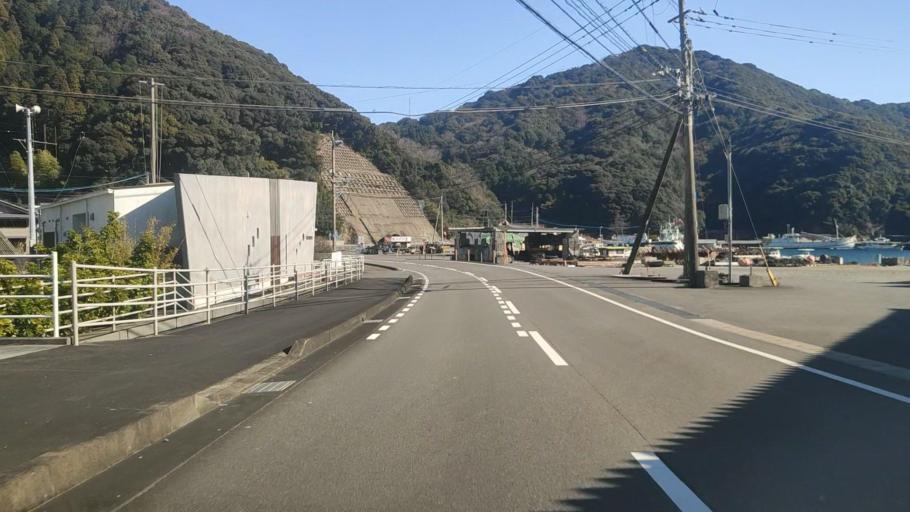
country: JP
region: Oita
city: Saiki
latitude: 32.7934
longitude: 131.9054
